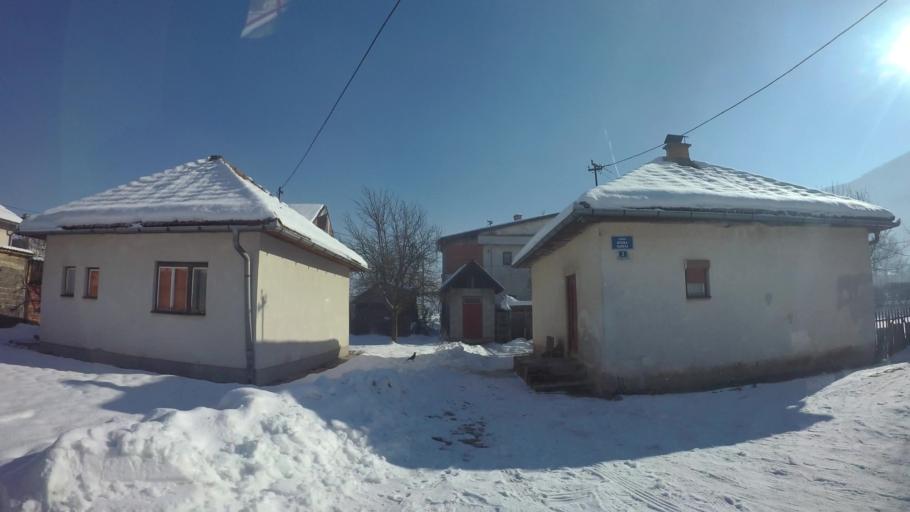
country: BA
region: Federation of Bosnia and Herzegovina
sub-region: Kanton Sarajevo
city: Sarajevo
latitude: 43.7914
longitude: 18.3393
